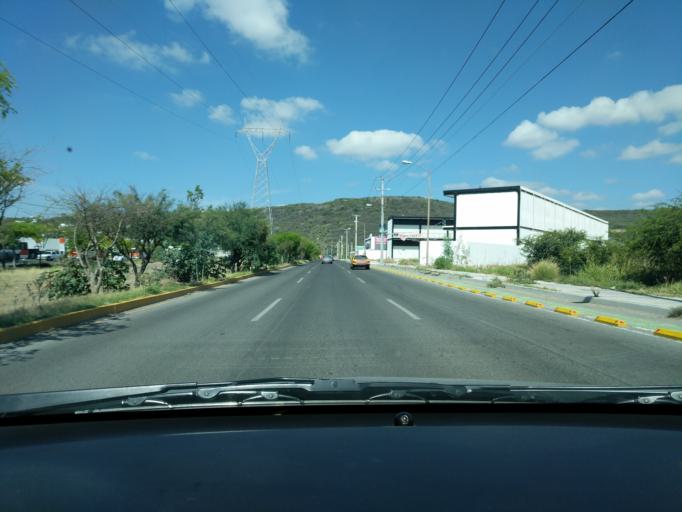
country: MX
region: Queretaro
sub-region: Queretaro
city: Patria Nueva
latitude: 20.6406
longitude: -100.4965
